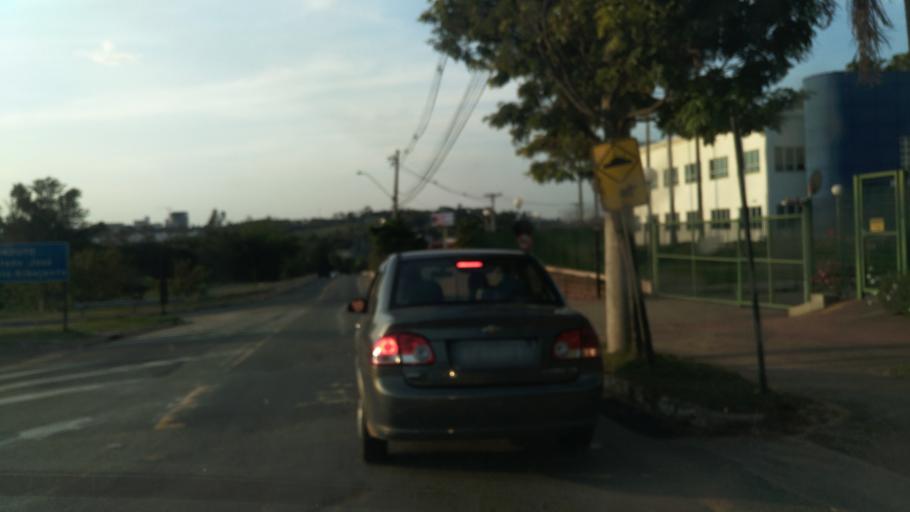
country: BR
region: Sao Paulo
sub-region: Valinhos
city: Valinhos
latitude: -22.9949
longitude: -47.0062
